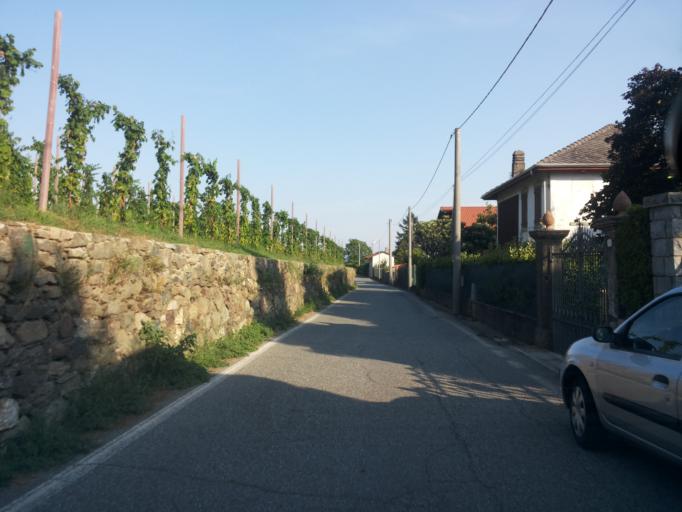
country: IT
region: Piedmont
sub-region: Provincia di Torino
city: Piverone
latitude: 45.4446
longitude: 8.0112
